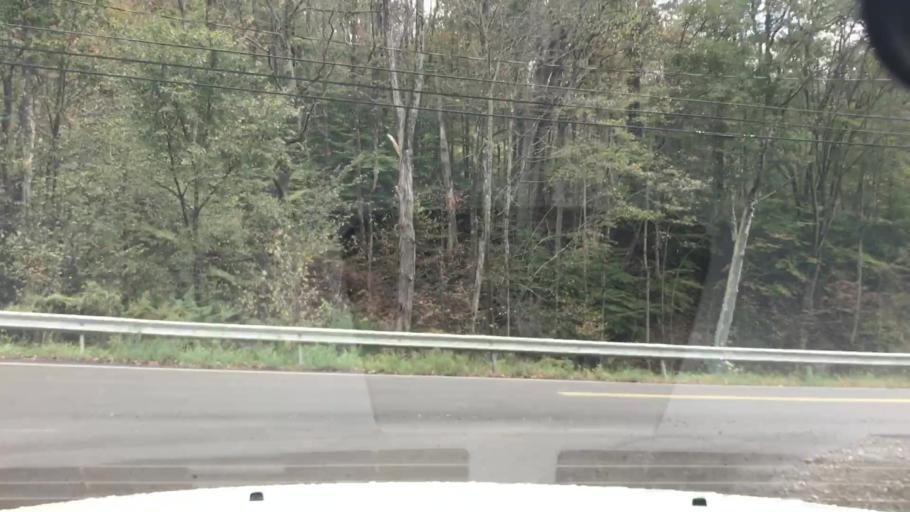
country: US
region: New York
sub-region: Cattaraugus County
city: Salamanca
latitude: 42.2631
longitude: -78.6770
